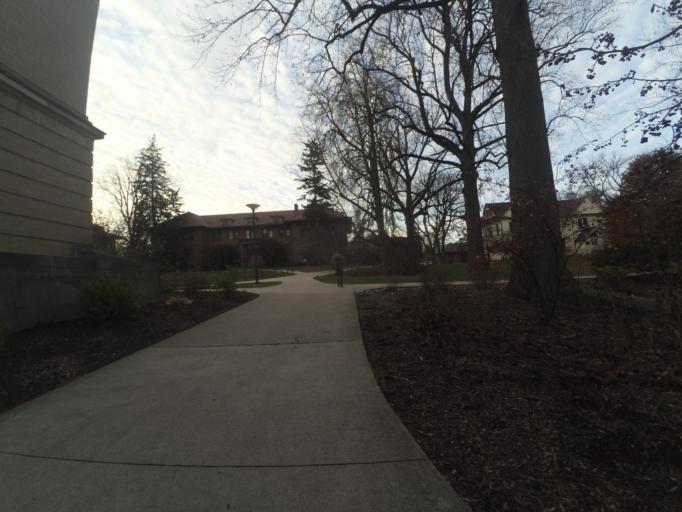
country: US
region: Pennsylvania
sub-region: Centre County
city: State College
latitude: 40.7998
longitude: -77.8637
